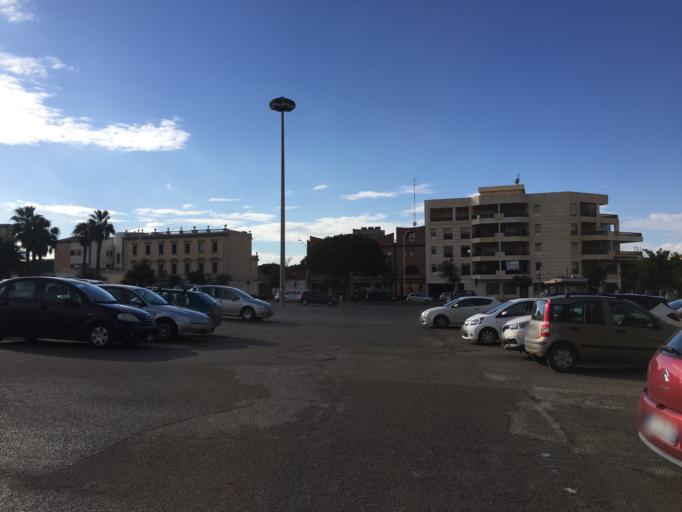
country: IT
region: Sardinia
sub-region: Provincia di Cagliari
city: Cagliari
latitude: 39.2097
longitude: 9.1224
